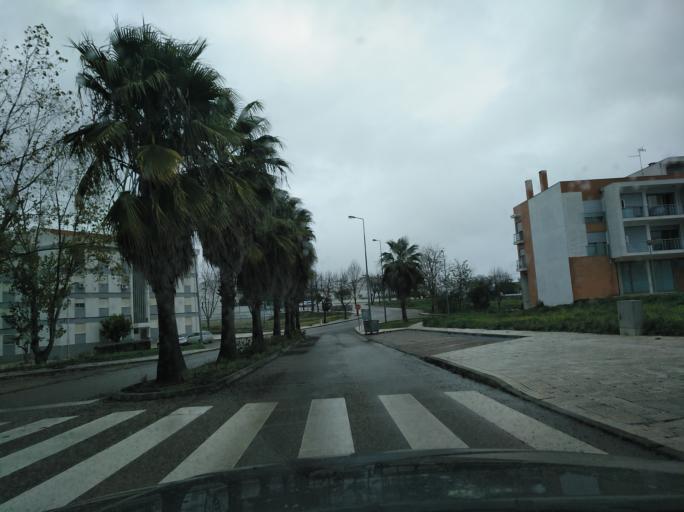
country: PT
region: Portalegre
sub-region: Elvas
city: Elvas
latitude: 38.8690
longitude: -7.1622
